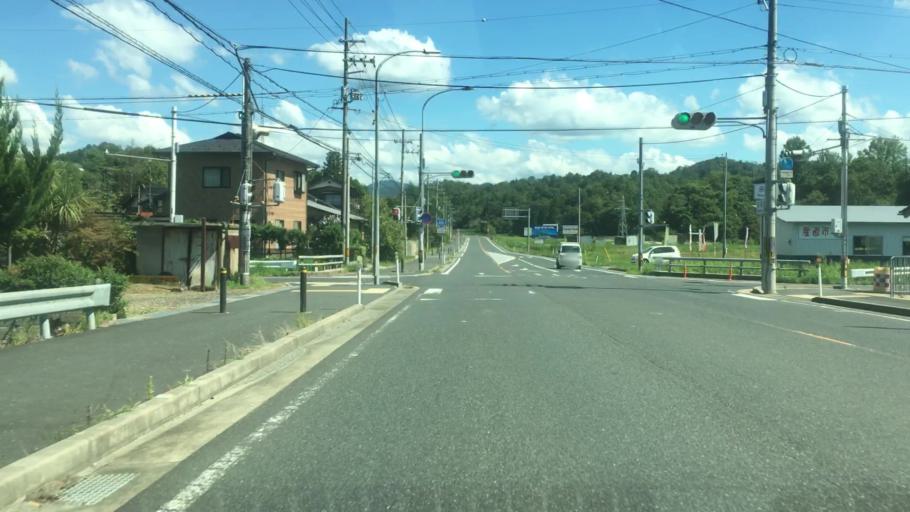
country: JP
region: Hyogo
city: Toyooka
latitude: 35.5896
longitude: 134.9421
